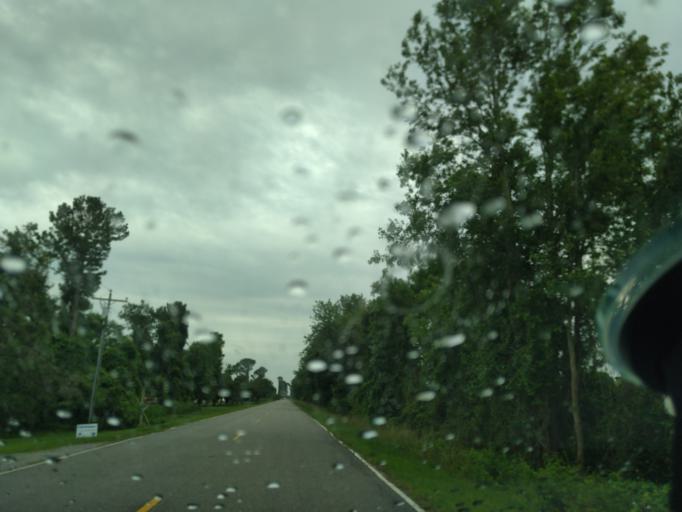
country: US
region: North Carolina
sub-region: Beaufort County
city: Belhaven
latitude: 35.7645
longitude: -76.5236
